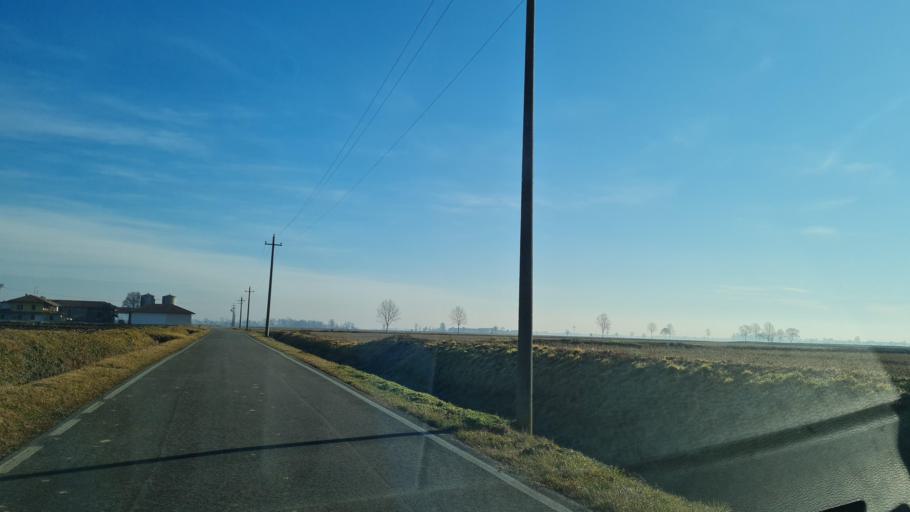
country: IT
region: Piedmont
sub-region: Provincia di Biella
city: Villanova Biellese
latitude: 45.4539
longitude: 8.1974
